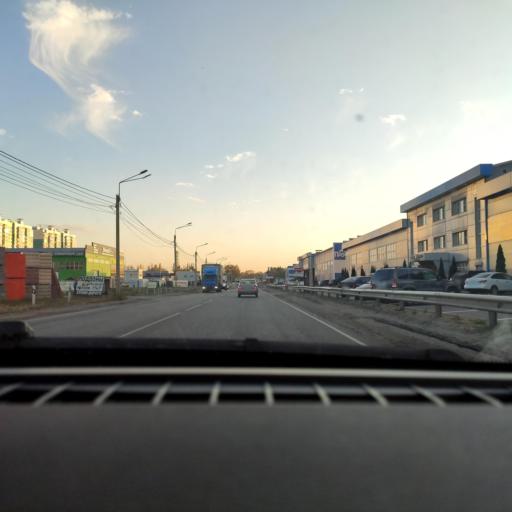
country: RU
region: Voronezj
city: Maslovka
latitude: 51.6390
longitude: 39.2929
